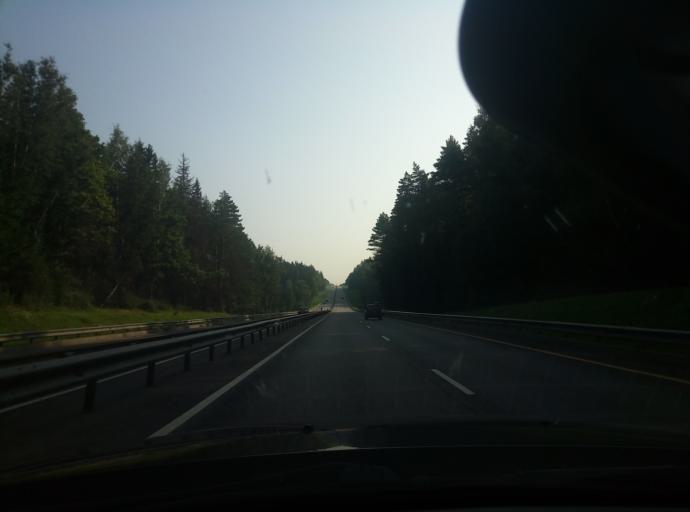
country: RU
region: Kaluga
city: Maloyaroslavets
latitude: 54.9999
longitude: 36.5273
